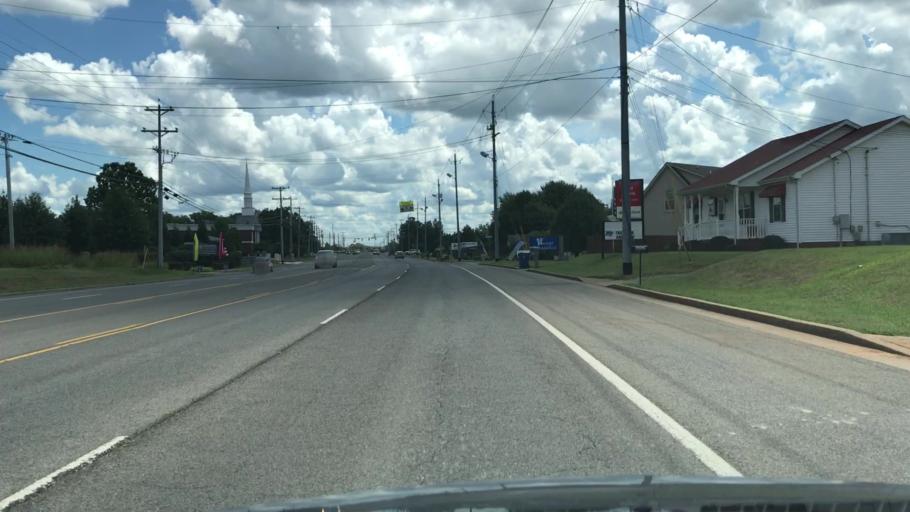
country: US
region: Tennessee
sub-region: Rutherford County
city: Murfreesboro
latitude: 35.8446
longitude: -86.4556
